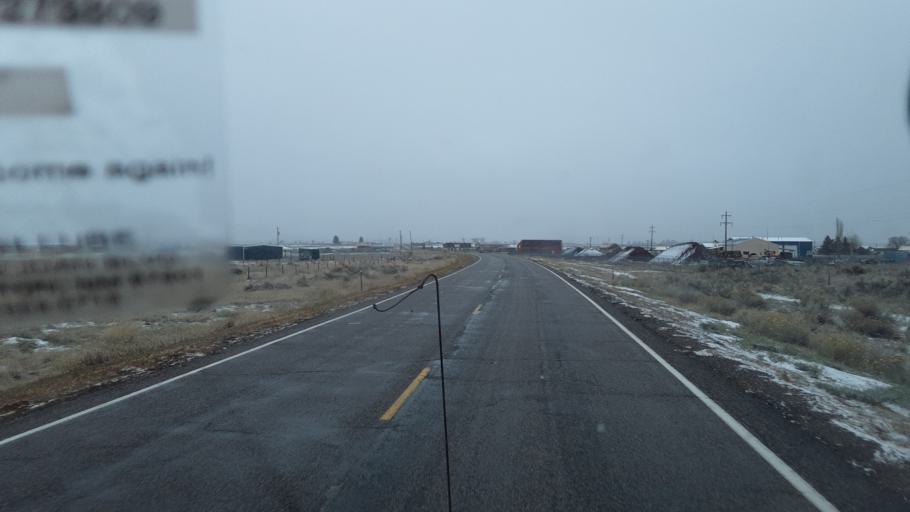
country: US
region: New Mexico
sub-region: Rio Arriba County
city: Tierra Amarilla
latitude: 36.7068
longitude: -106.5580
